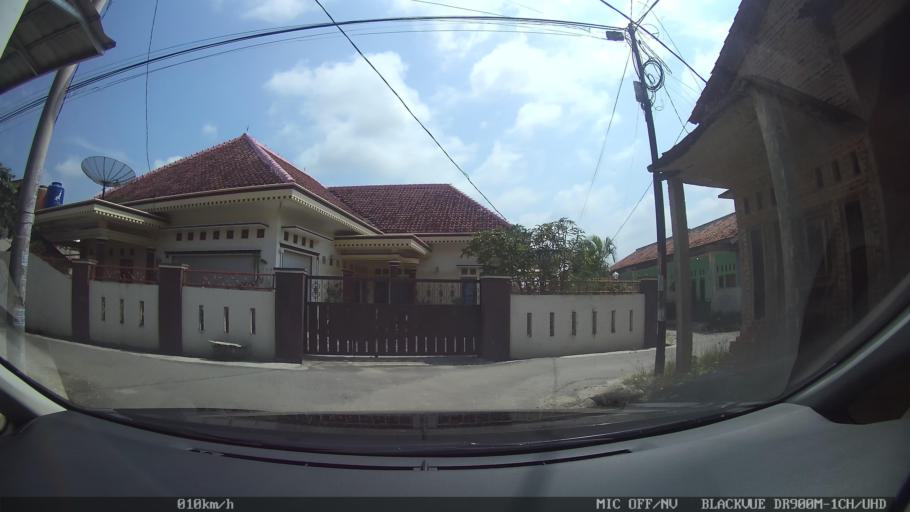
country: ID
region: Lampung
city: Kedaton
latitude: -5.3554
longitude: 105.2819
